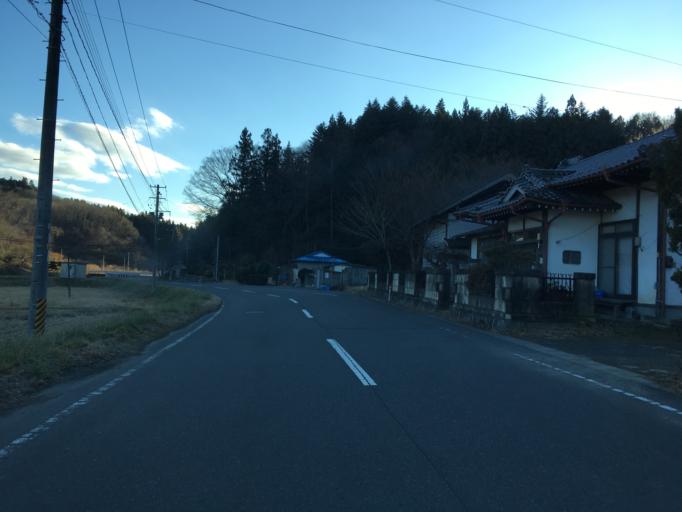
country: JP
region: Fukushima
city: Ishikawa
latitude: 37.1839
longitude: 140.5548
